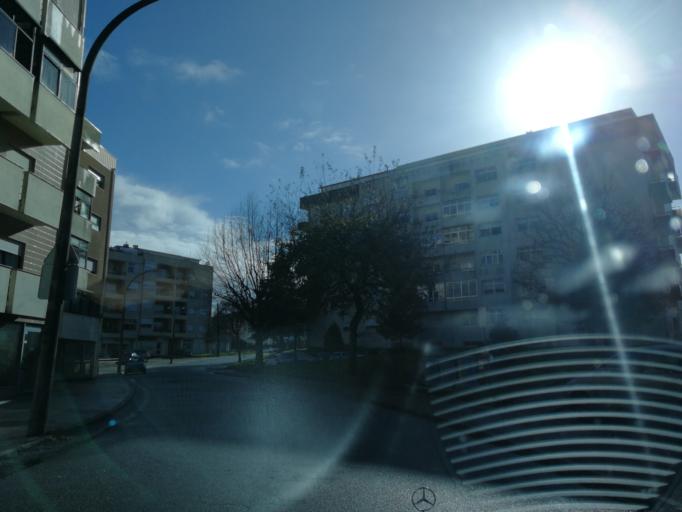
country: PT
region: Braga
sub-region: Braga
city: Braga
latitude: 41.5442
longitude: -8.4074
